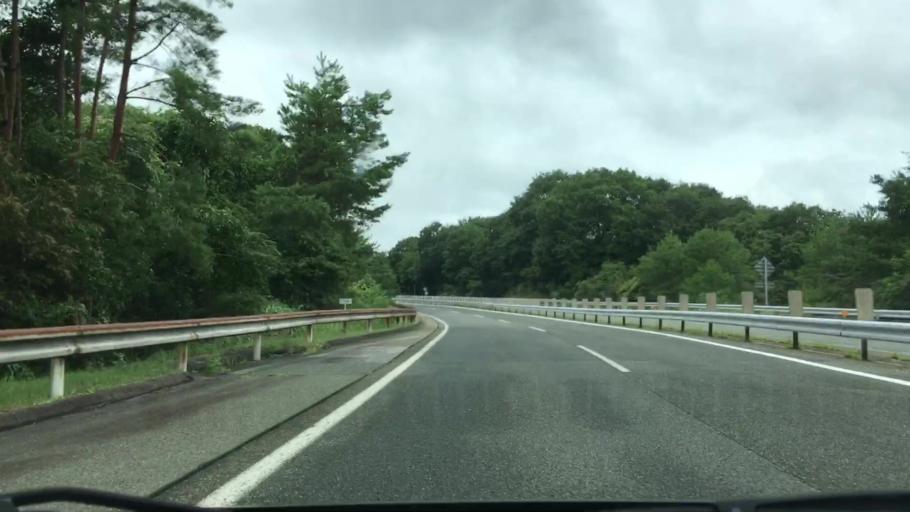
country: JP
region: Hiroshima
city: Shobara
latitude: 34.8719
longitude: 133.1551
